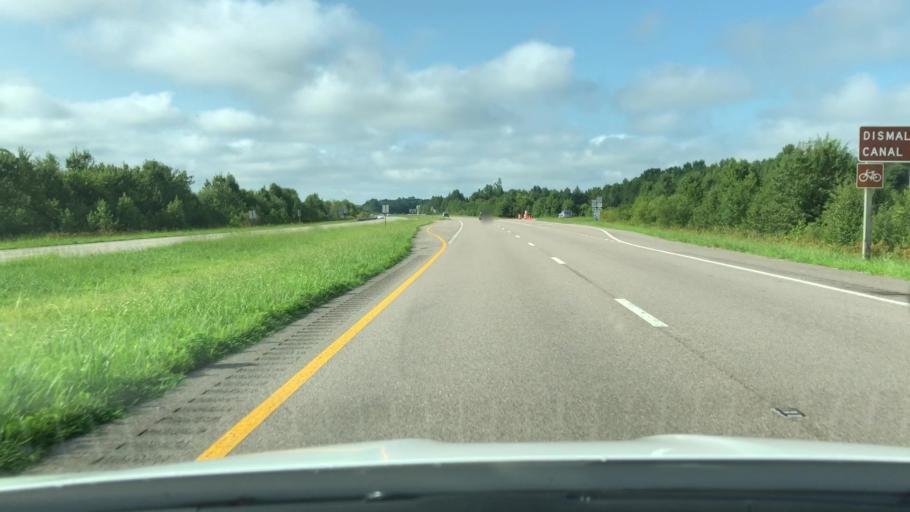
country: US
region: Virginia
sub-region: City of Portsmouth
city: Portsmouth Heights
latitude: 36.6902
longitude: -76.3470
